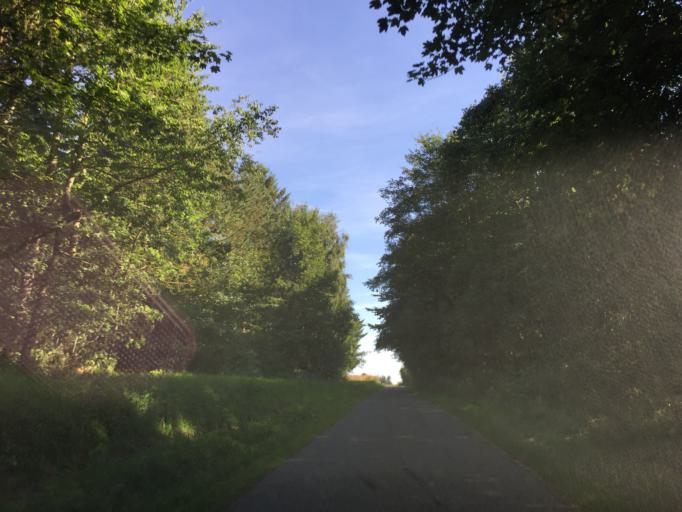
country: DK
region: Central Jutland
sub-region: Viborg Kommune
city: Bjerringbro
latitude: 56.2866
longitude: 9.6838
